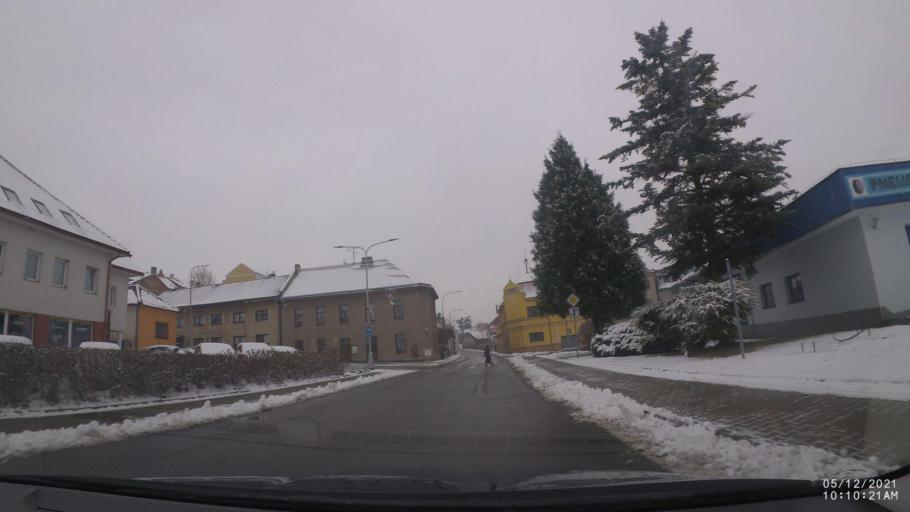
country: CZ
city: Kostelec nad Orlici
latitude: 50.1220
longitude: 16.2092
